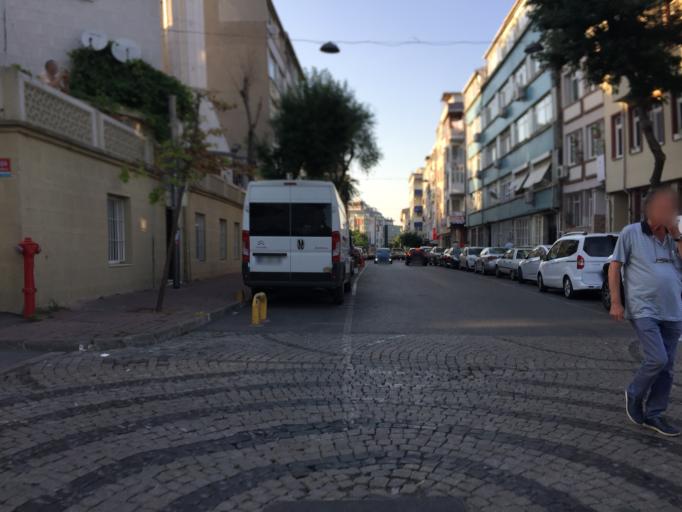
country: TR
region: Istanbul
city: Istanbul
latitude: 41.0094
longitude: 28.9410
